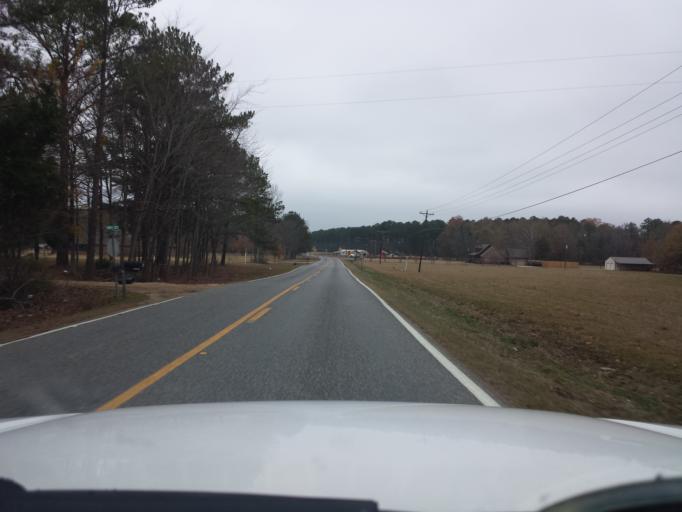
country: US
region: Mississippi
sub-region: Madison County
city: Canton
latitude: 32.4949
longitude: -89.9238
